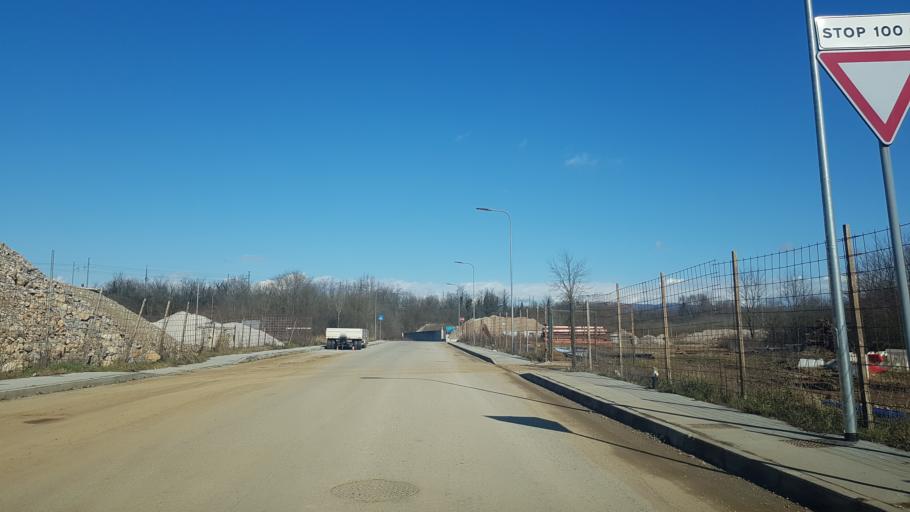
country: IT
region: Friuli Venezia Giulia
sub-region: Provincia di Gorizia
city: Savogna d'Isonzo
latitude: 45.8981
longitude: 13.5745
